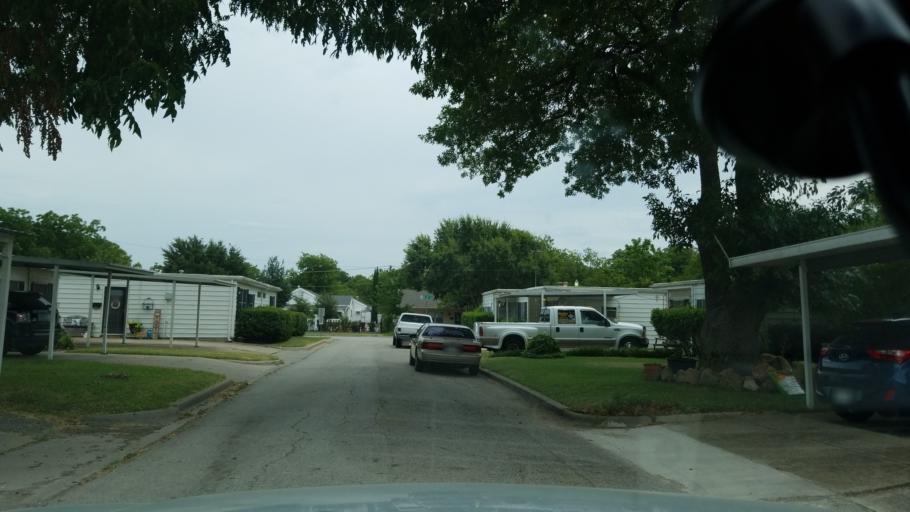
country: US
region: Texas
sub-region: Dallas County
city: Grand Prairie
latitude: 32.7409
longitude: -96.9933
